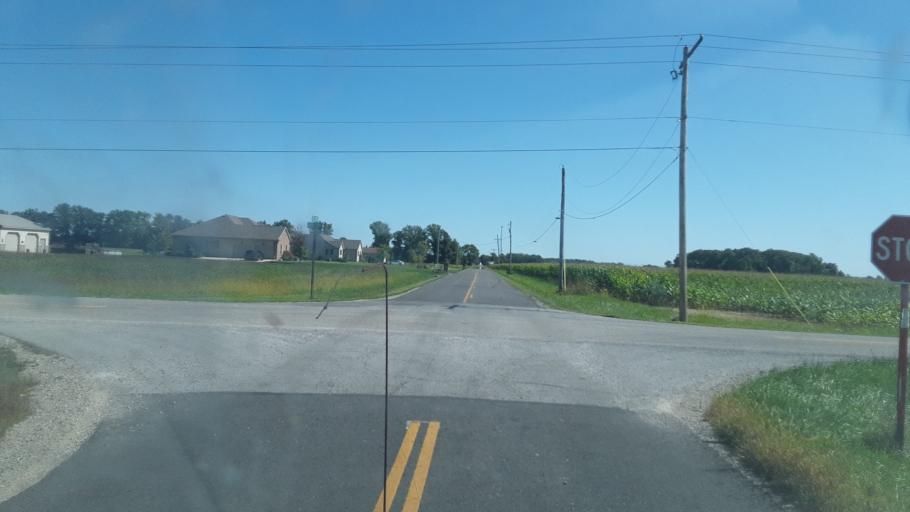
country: US
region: Ohio
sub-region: Huron County
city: Bellevue
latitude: 41.2116
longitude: -82.8605
